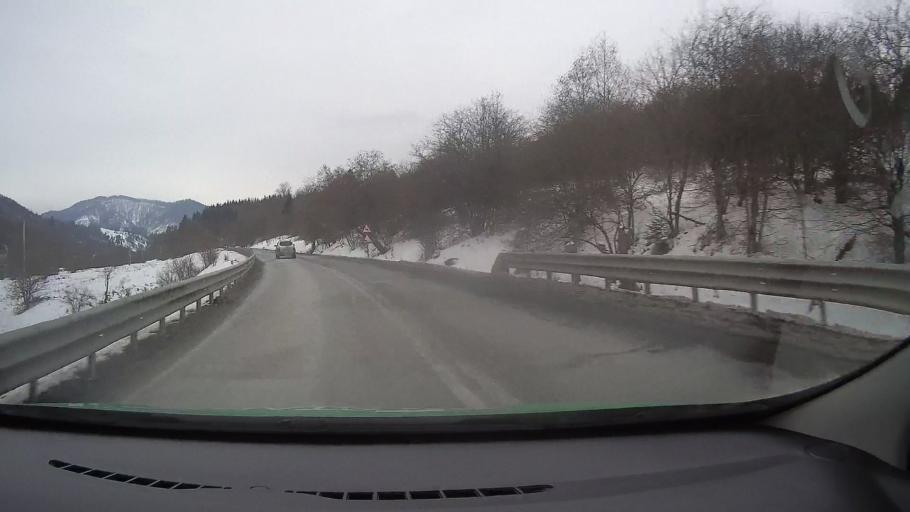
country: RO
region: Brasov
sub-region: Oras Predeal
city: Predeal
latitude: 45.5278
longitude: 25.4997
